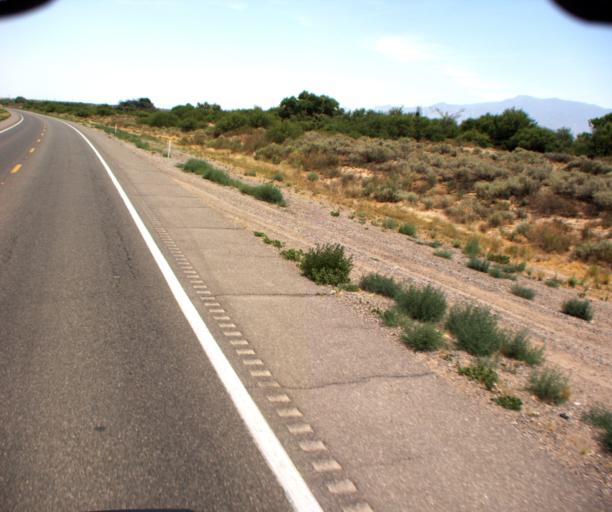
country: US
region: Arizona
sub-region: Graham County
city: Pima
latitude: 32.9403
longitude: -109.9063
